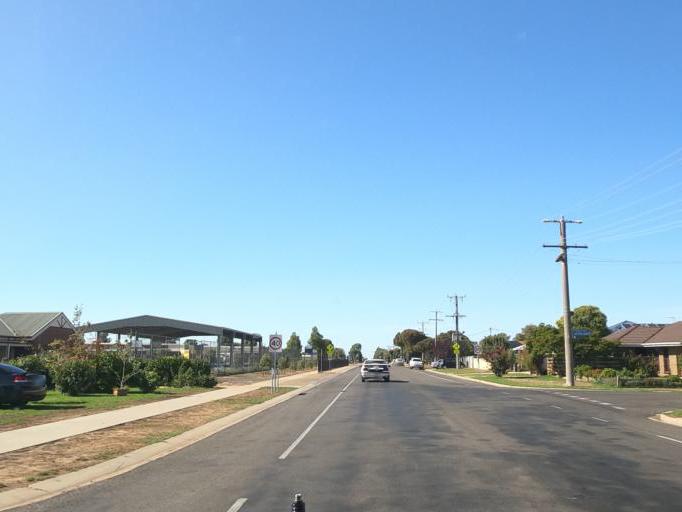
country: AU
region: Victoria
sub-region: Moira
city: Yarrawonga
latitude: -36.0108
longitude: 146.0132
